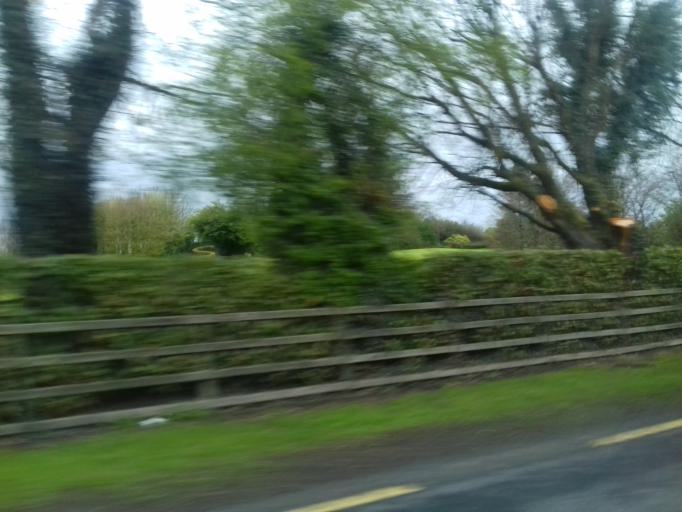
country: IE
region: Ulster
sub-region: An Cabhan
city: Ballyconnell
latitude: 54.0941
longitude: -7.5528
